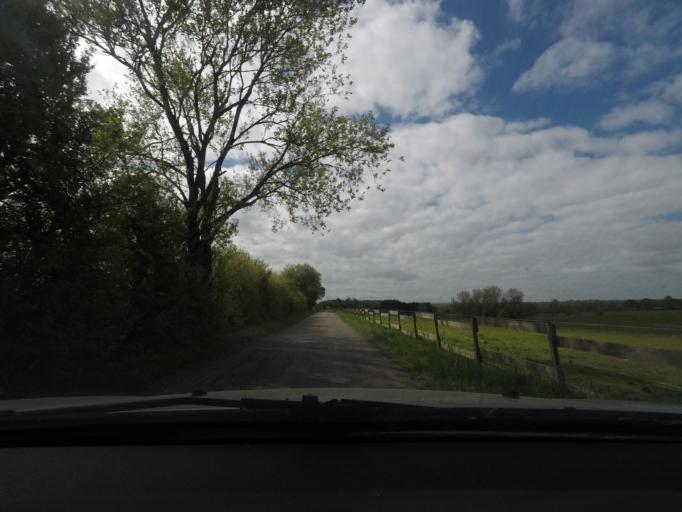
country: BE
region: Wallonia
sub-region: Province du Luxembourg
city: Habay-la-Vieille
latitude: 49.7132
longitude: 5.5977
